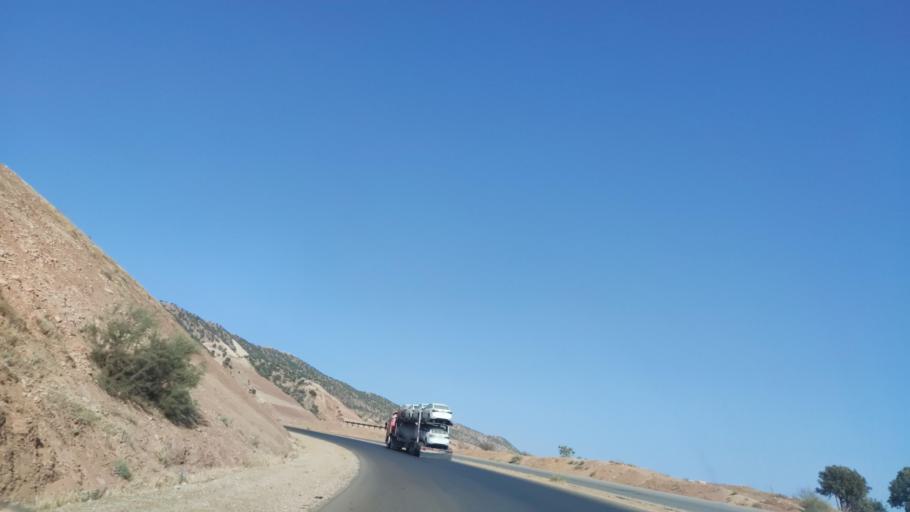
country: IQ
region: Arbil
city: Shaqlawah
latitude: 36.4327
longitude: 44.3109
